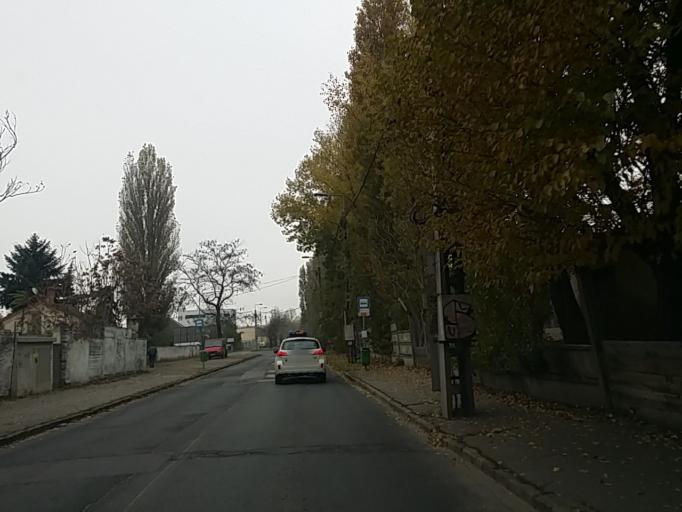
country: HU
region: Budapest
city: Budapest IV. keruelet
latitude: 47.5452
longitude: 19.0957
